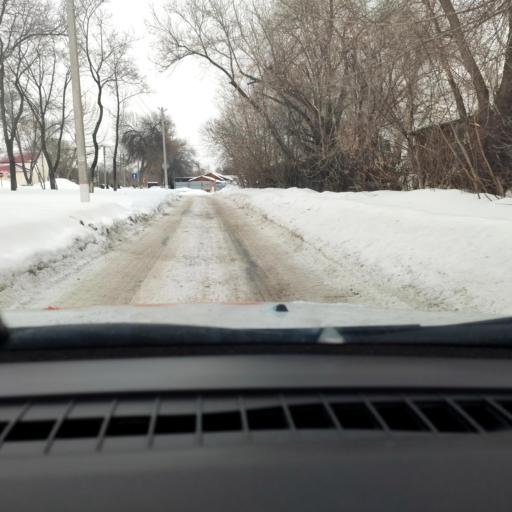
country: RU
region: Samara
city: Novokuybyshevsk
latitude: 53.1148
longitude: 49.9355
